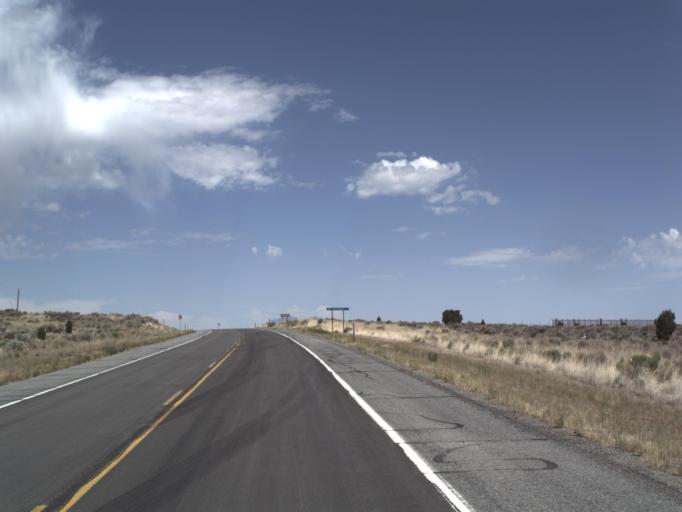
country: US
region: Utah
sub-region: Utah County
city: Eagle Mountain
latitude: 40.0490
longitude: -112.2951
